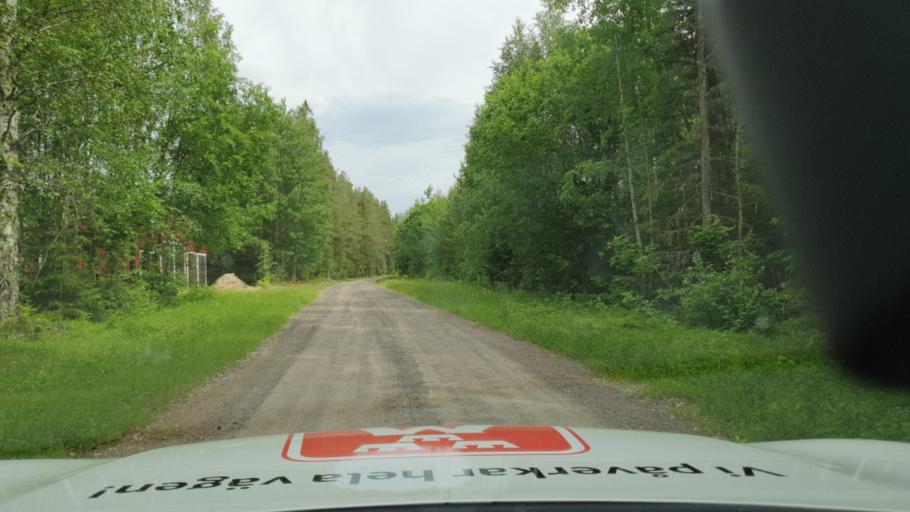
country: SE
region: Vaesterbotten
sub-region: Robertsfors Kommun
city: Robertsfors
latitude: 64.2605
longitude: 20.6612
